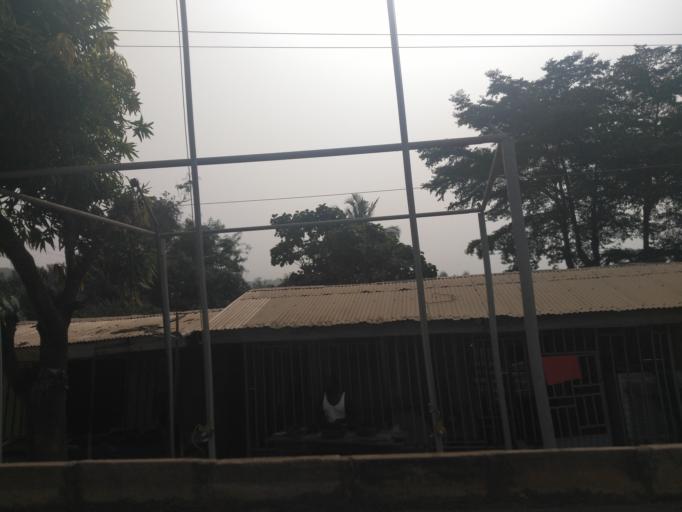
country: GH
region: Ashanti
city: Kumasi
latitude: 6.7132
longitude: -1.6425
